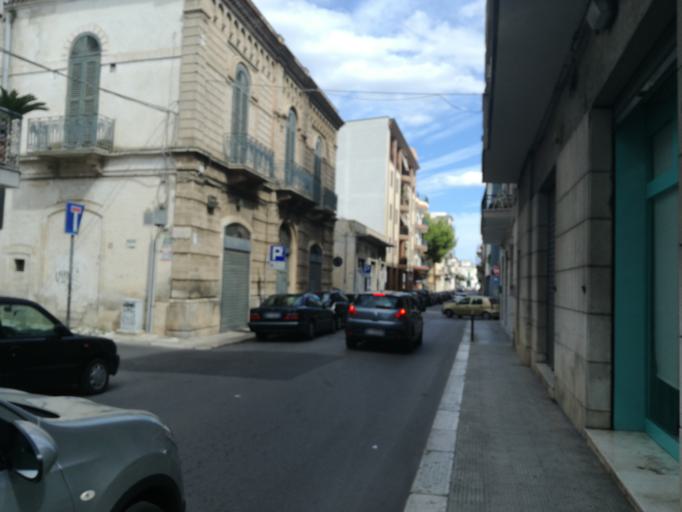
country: IT
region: Apulia
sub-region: Provincia di Bari
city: Triggiano
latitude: 41.0631
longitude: 16.9176
